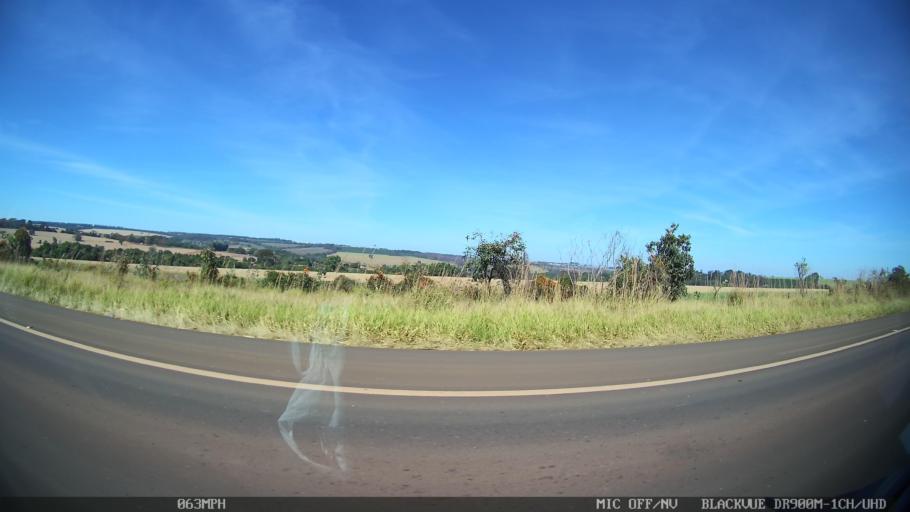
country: BR
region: Sao Paulo
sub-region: Franca
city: Franca
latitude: -20.5535
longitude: -47.4914
